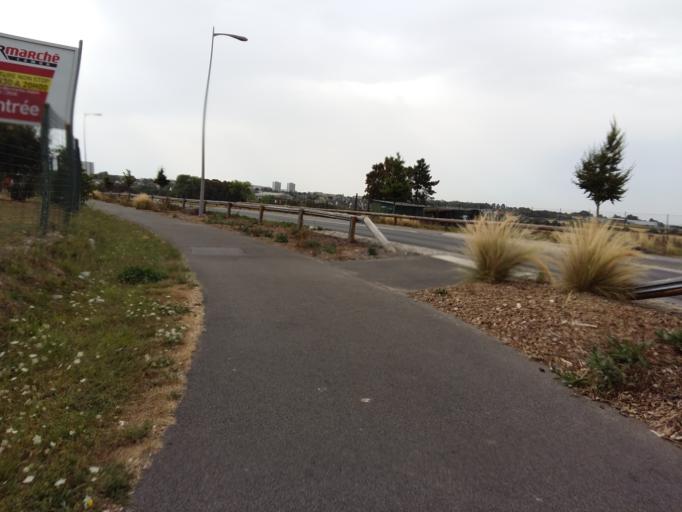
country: FR
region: Picardie
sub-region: Departement de la Somme
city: Camon
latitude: 49.9009
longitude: 2.3408
